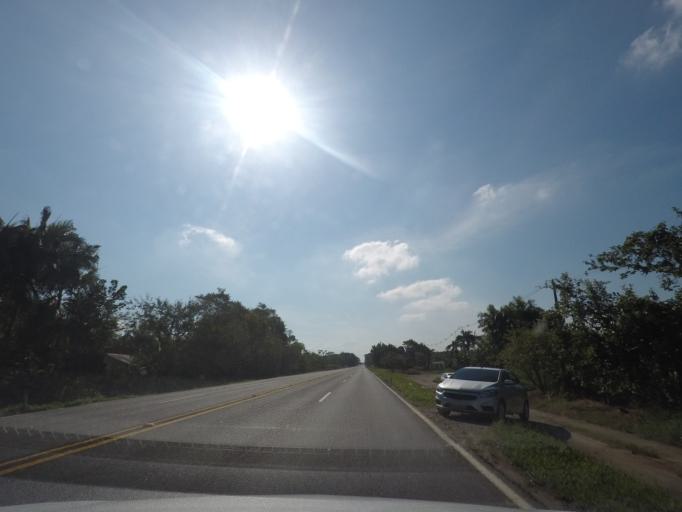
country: BR
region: Parana
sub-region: Pontal Do Parana
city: Pontal do Parana
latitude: -25.6475
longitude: -48.5890
